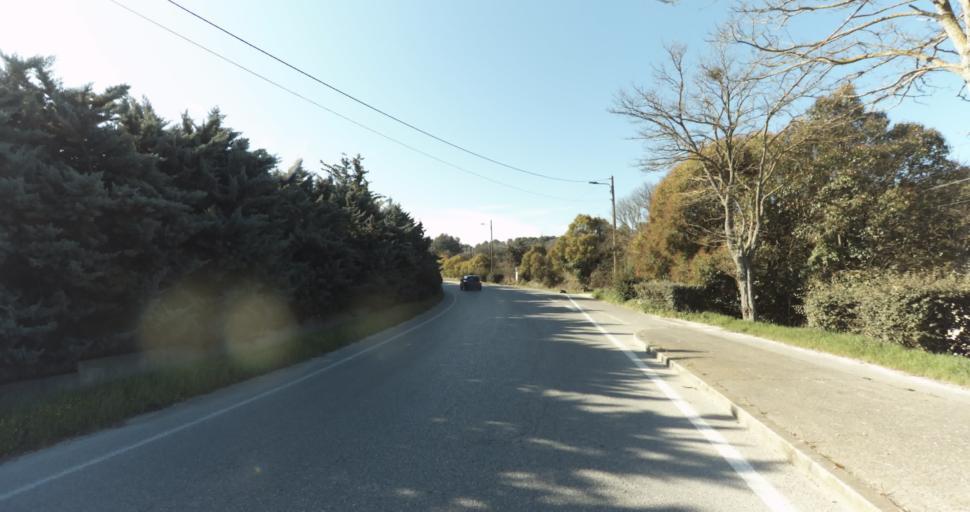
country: FR
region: Provence-Alpes-Cote d'Azur
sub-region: Departement des Bouches-du-Rhone
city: Aix-en-Provence
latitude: 43.5577
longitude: 5.4337
